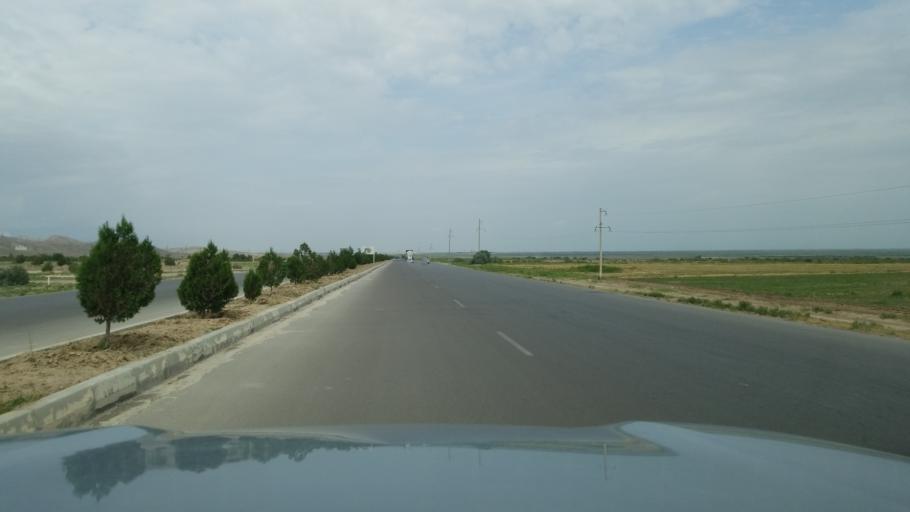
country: TM
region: Ahal
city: Baharly
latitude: 38.2375
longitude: 57.7731
